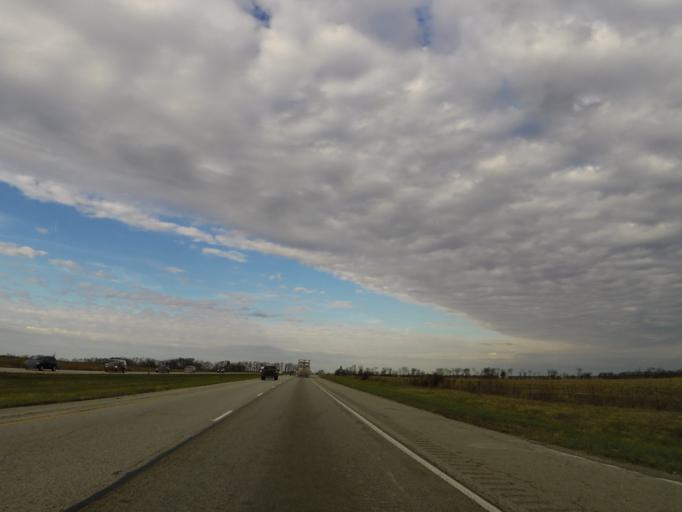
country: US
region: Illinois
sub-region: Washington County
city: Nashville
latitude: 38.4141
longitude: -89.4366
